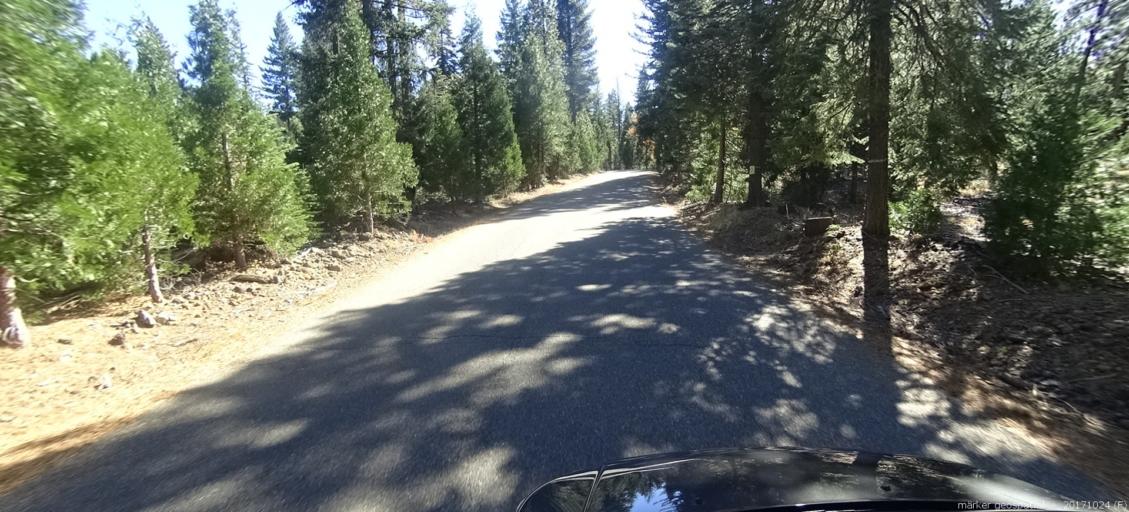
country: US
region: California
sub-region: Shasta County
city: Shingletown
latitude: 40.5112
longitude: -121.6692
